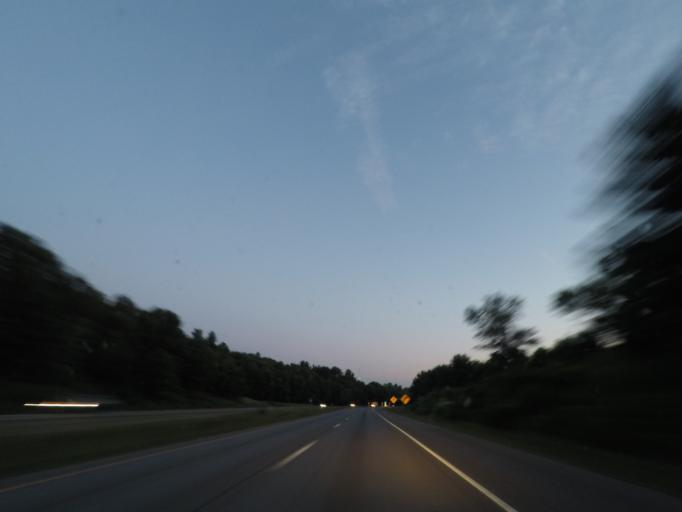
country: US
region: Connecticut
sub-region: Windham County
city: Putnam
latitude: 41.9091
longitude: -71.8919
